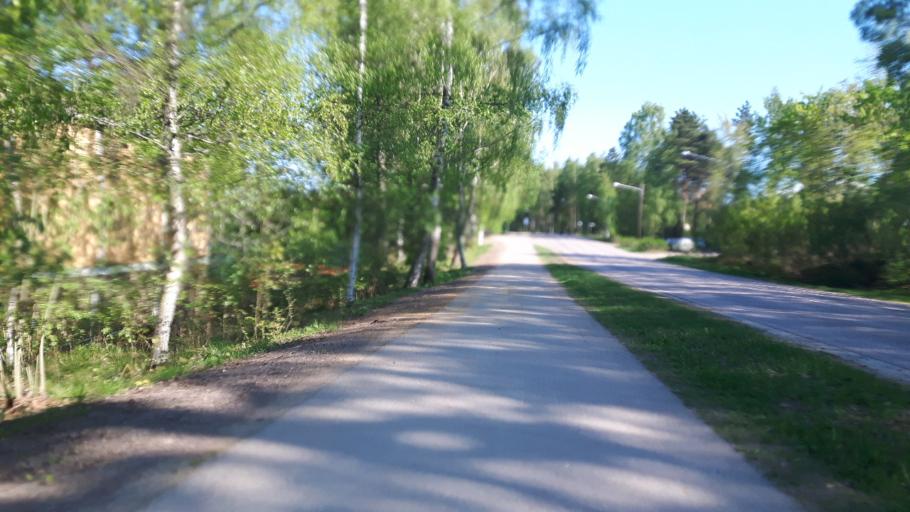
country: FI
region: Kymenlaakso
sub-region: Kotka-Hamina
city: Kotka
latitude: 60.4761
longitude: 26.8705
